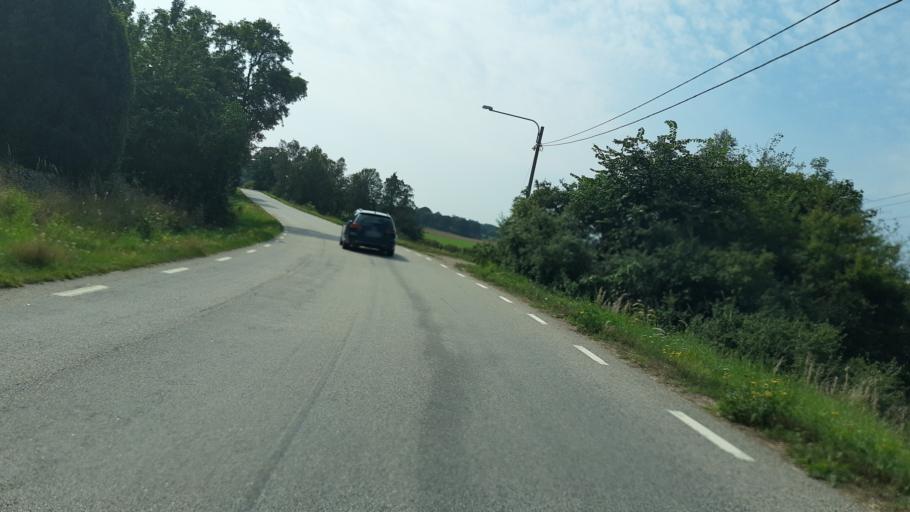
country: SE
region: Blekinge
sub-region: Ronneby Kommun
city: Kallinge
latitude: 56.2163
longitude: 15.3563
